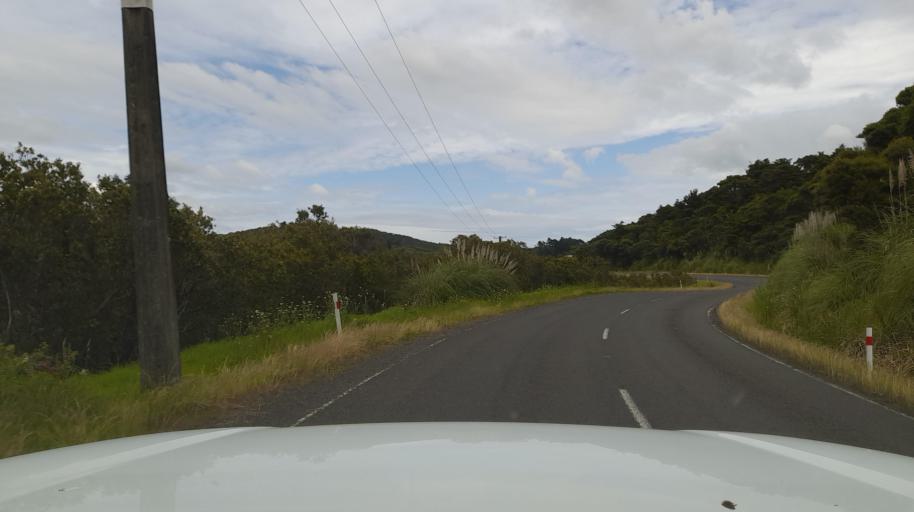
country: NZ
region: Northland
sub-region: Far North District
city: Kaitaia
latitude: -35.3996
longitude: 173.3833
